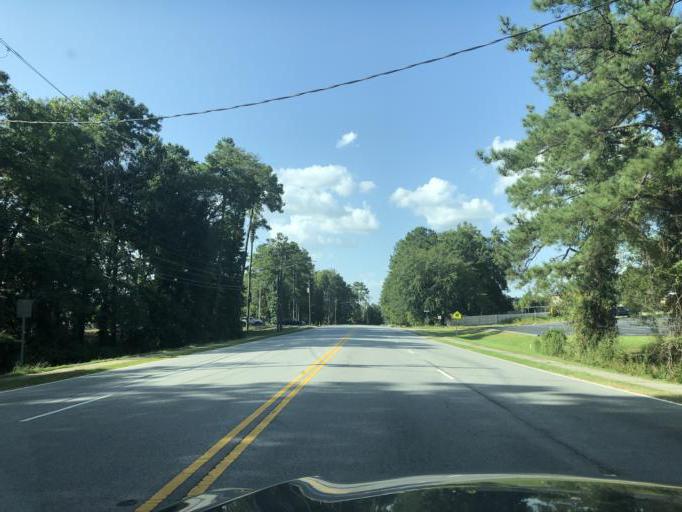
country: US
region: Georgia
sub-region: Muscogee County
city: Columbus
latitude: 32.4866
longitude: -84.8965
